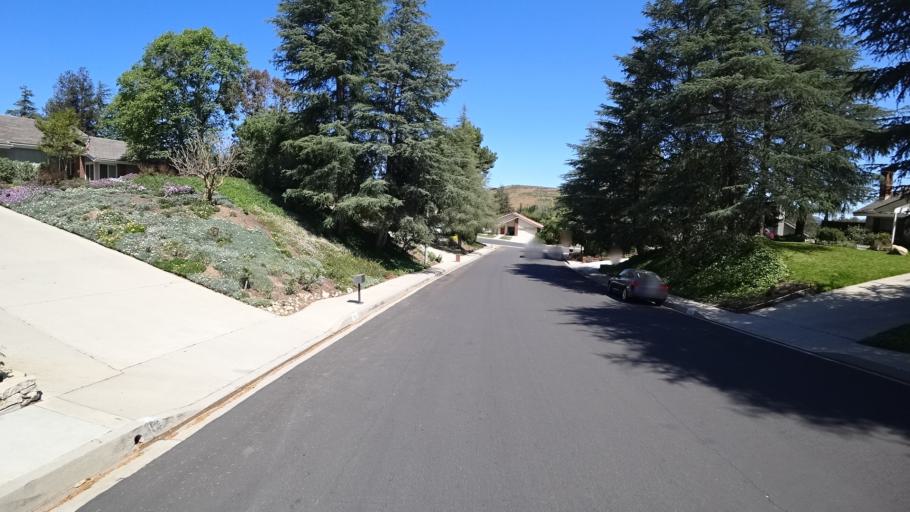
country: US
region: California
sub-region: Ventura County
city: Casa Conejo
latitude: 34.2034
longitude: -118.8908
